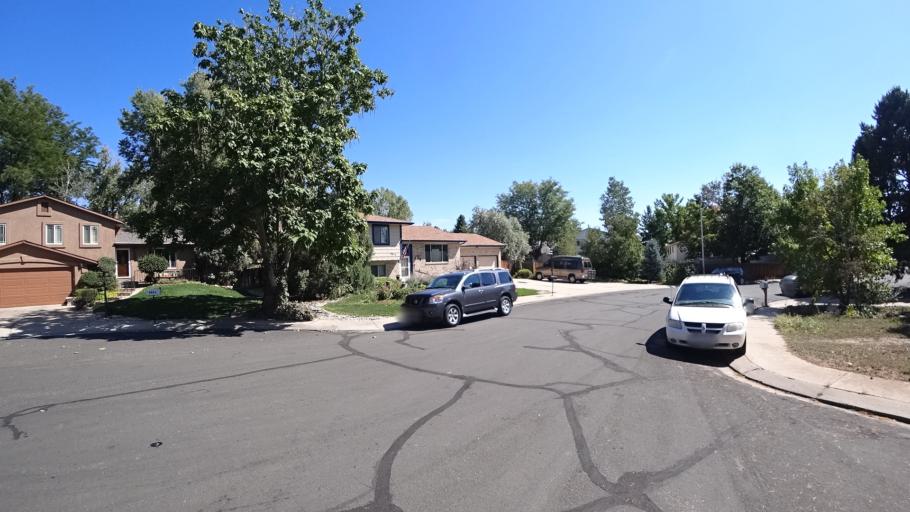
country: US
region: Colorado
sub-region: El Paso County
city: Cimarron Hills
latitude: 38.9050
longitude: -104.7614
